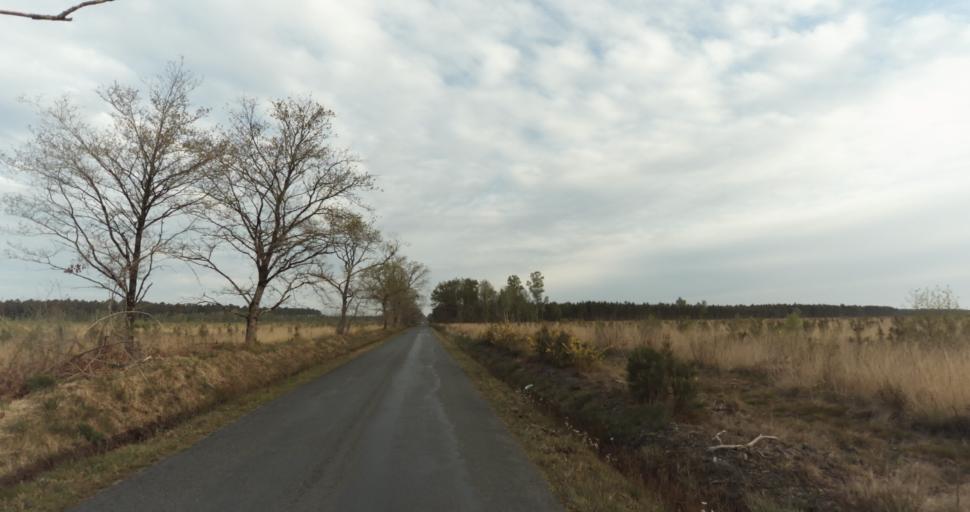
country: FR
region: Aquitaine
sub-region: Departement de la Gironde
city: Saint-Aubin-de-Medoc
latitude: 44.7834
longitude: -0.7492
